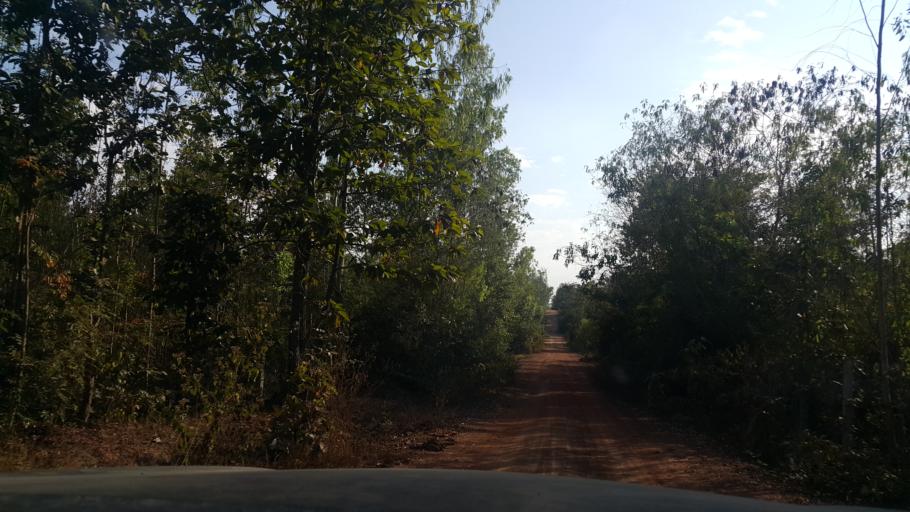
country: TH
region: Lampang
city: Hang Chat
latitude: 18.2828
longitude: 99.3575
